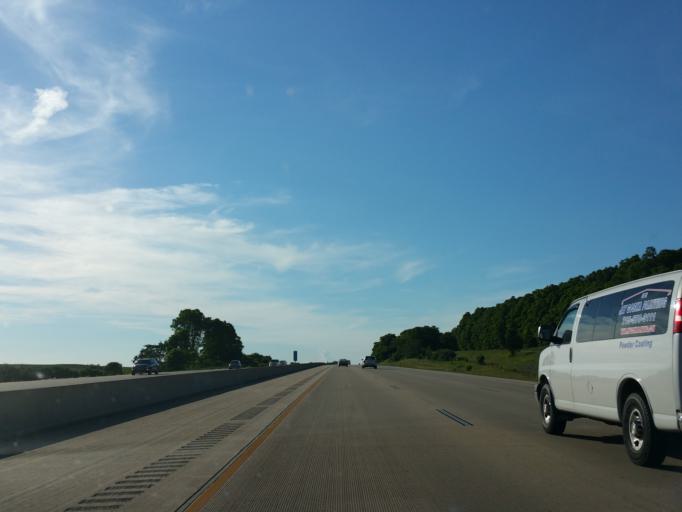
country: US
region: Wisconsin
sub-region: Columbia County
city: Poynette
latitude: 43.3166
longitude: -89.4414
